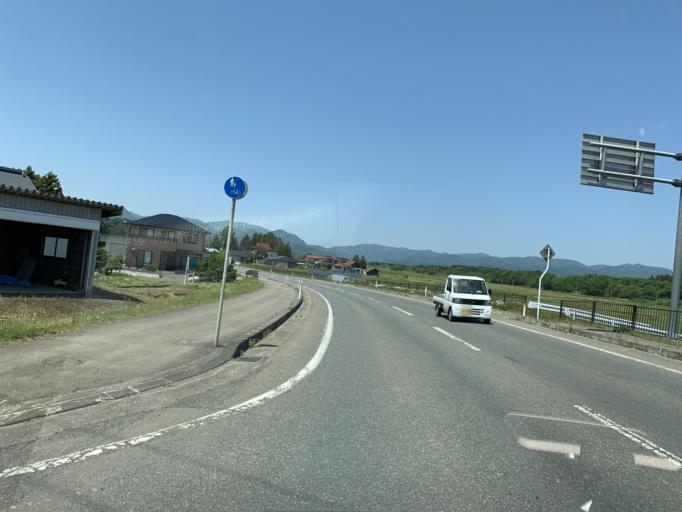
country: JP
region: Iwate
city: Kitakami
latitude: 39.2840
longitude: 141.0479
